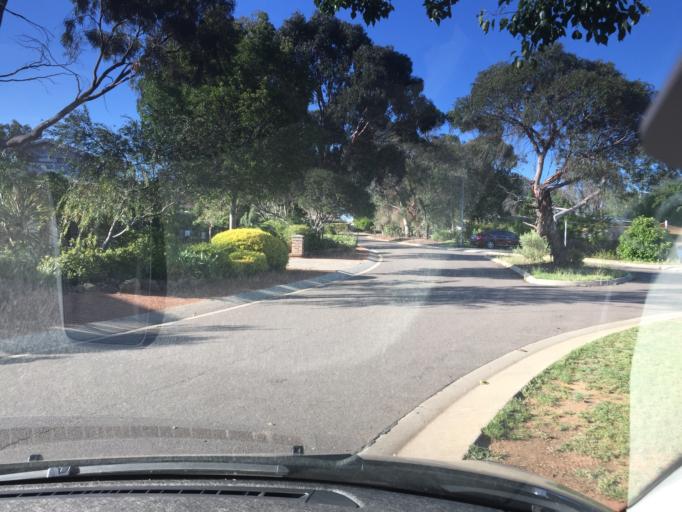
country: AU
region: Australian Capital Territory
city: Kaleen
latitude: -35.2177
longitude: 149.1151
